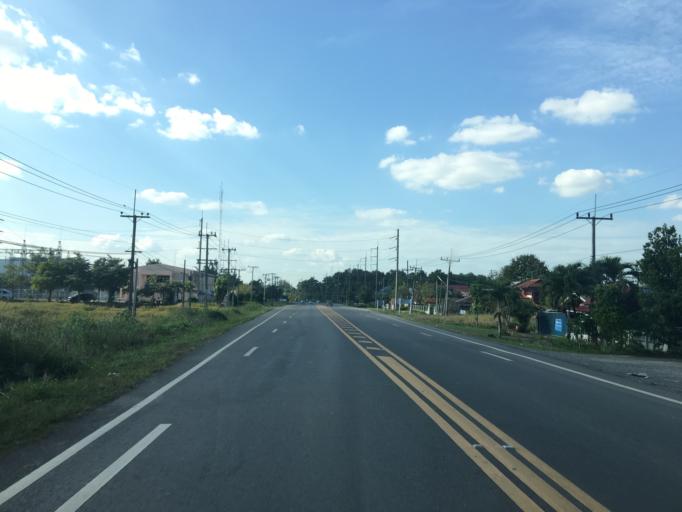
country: TH
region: Phayao
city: Chun
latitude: 19.3321
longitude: 100.1392
